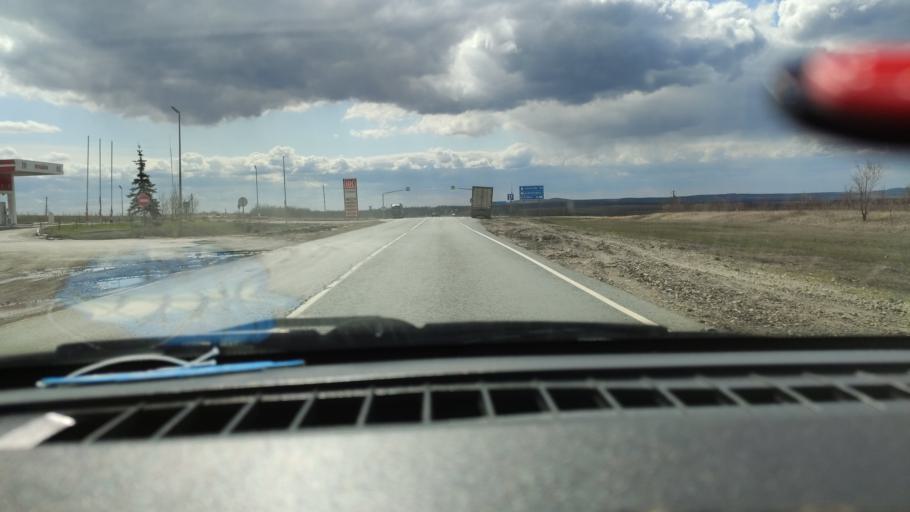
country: RU
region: Saratov
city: Alekseyevka
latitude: 52.2908
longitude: 47.9298
